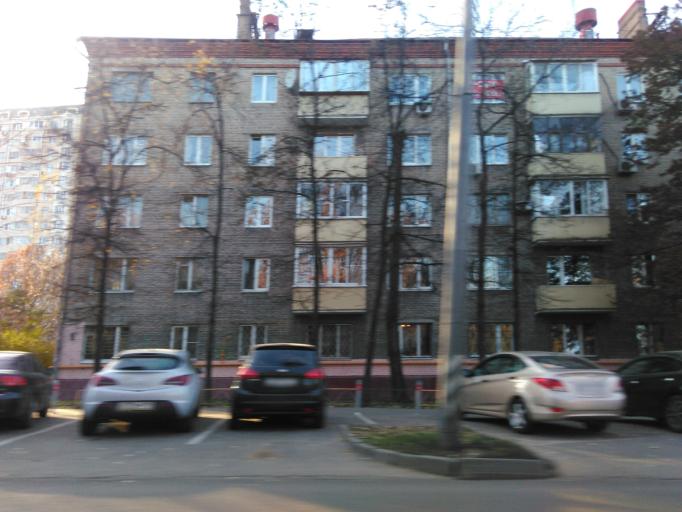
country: RU
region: Moscow
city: Ostankinskiy
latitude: 55.8271
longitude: 37.6017
